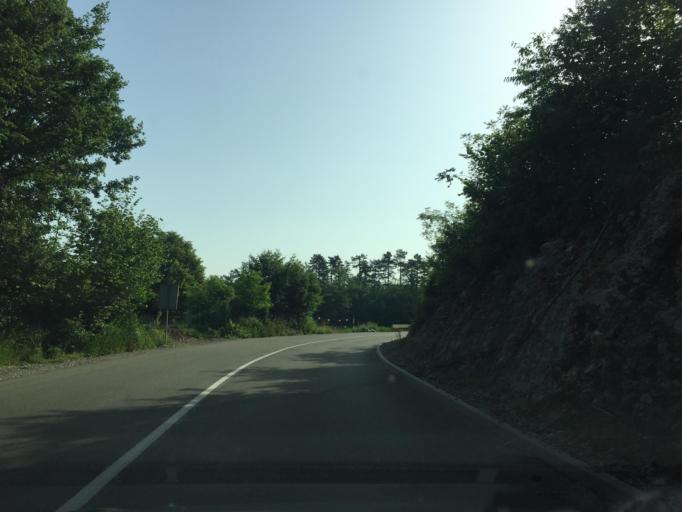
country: HR
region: Primorsko-Goranska
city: Matulji
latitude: 45.4130
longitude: 14.2932
